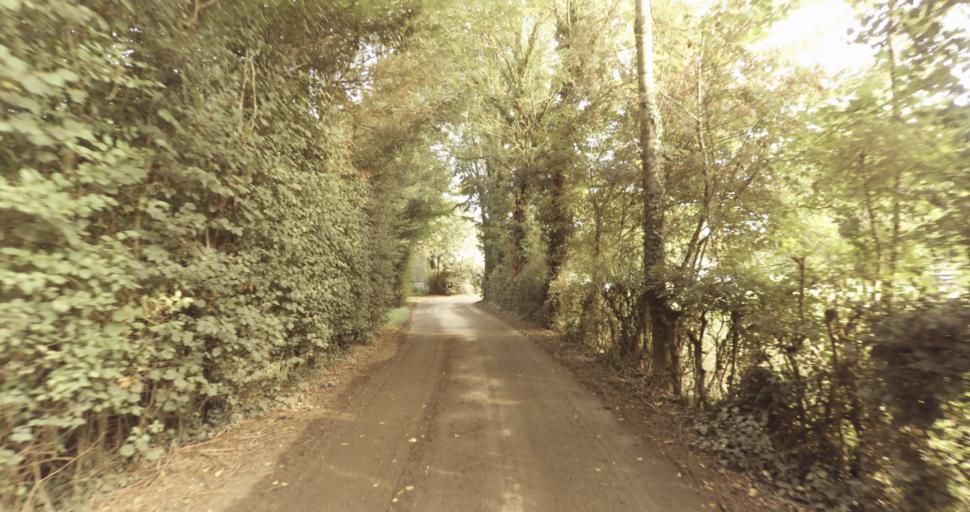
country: FR
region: Lower Normandy
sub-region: Departement de l'Orne
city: Vimoutiers
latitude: 48.8943
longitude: 0.2302
